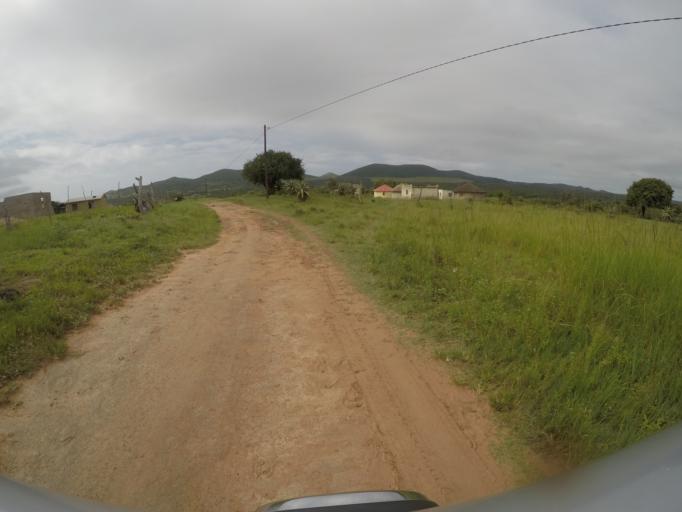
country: ZA
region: KwaZulu-Natal
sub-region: uThungulu District Municipality
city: Empangeni
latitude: -28.6147
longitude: 31.8455
